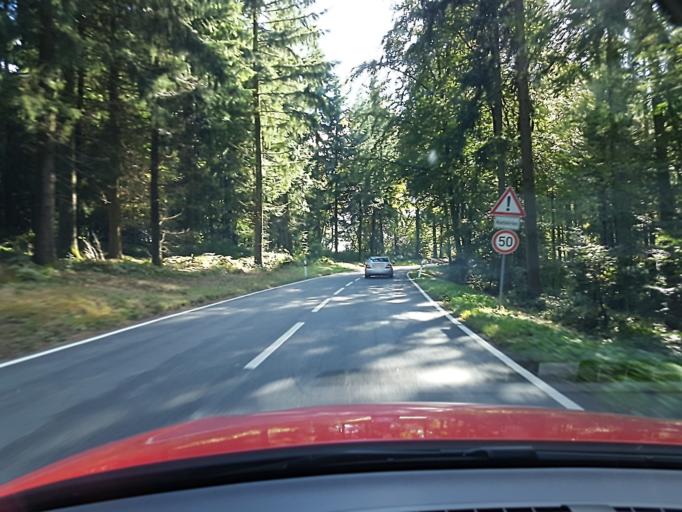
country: DE
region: Baden-Wuerttemberg
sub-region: Karlsruhe Region
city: Wilhelmsfeld
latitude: 49.4604
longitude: 8.7523
